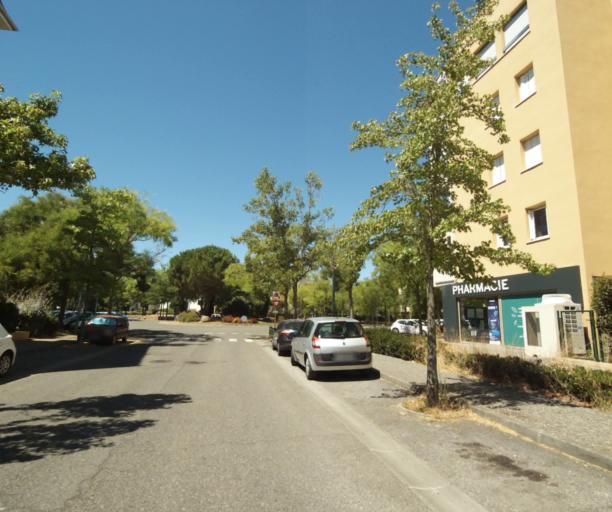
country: FR
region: Midi-Pyrenees
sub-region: Departement de la Haute-Garonne
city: Castanet-Tolosan
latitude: 43.5175
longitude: 1.5086
